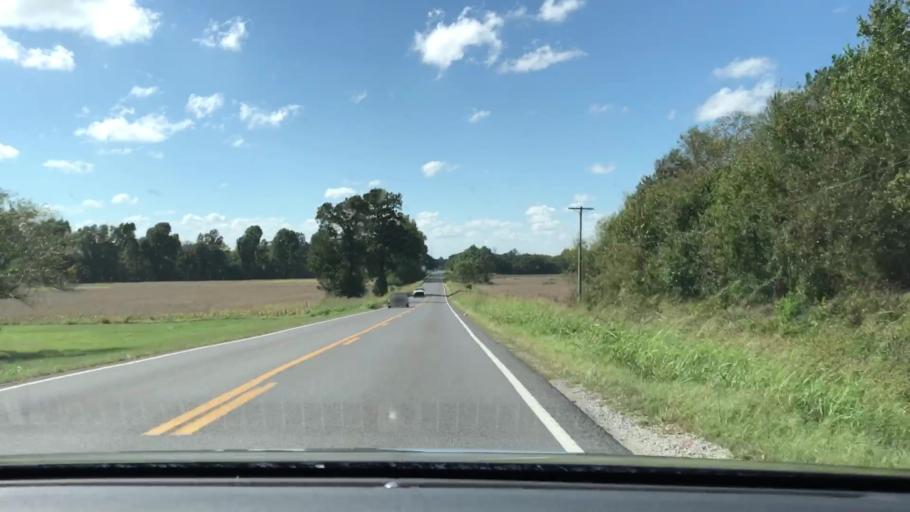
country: US
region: Kentucky
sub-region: Graves County
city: Mayfield
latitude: 36.7527
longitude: -88.6112
